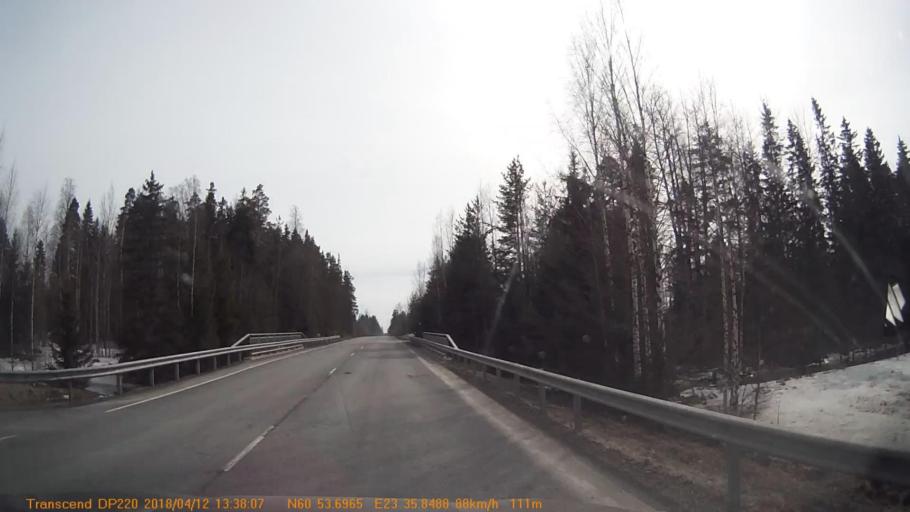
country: FI
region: Haeme
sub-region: Forssa
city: Forssa
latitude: 60.8946
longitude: 23.5976
